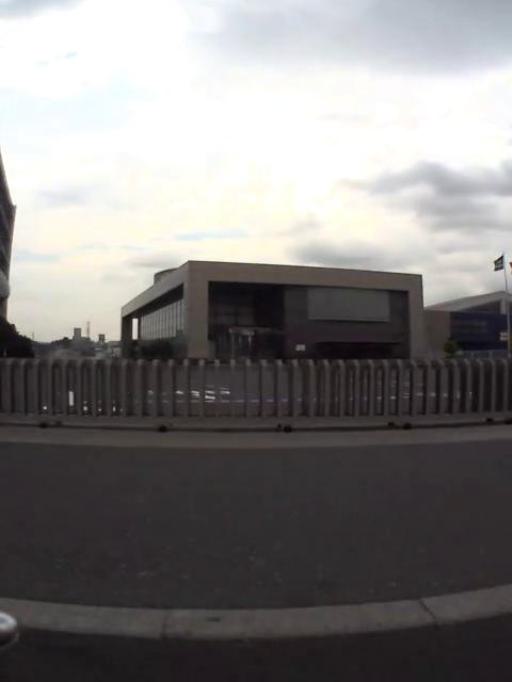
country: JP
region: Osaka
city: Neyagawa
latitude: 34.7588
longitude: 135.6275
